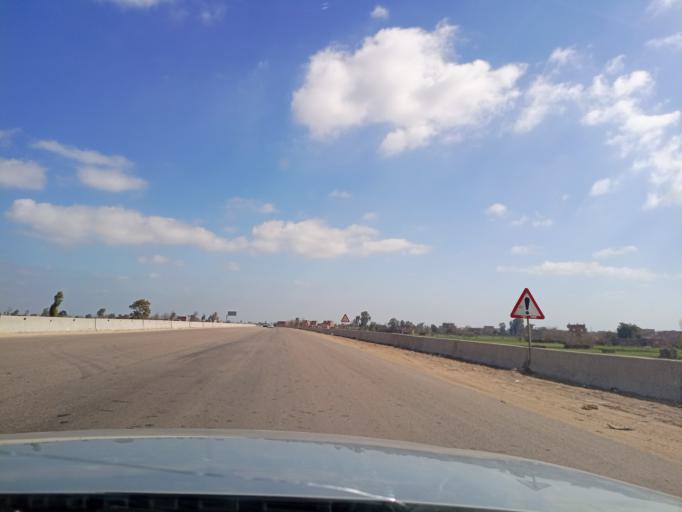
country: EG
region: Muhafazat al Minufiyah
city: Al Bajur
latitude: 30.3894
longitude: 30.9904
